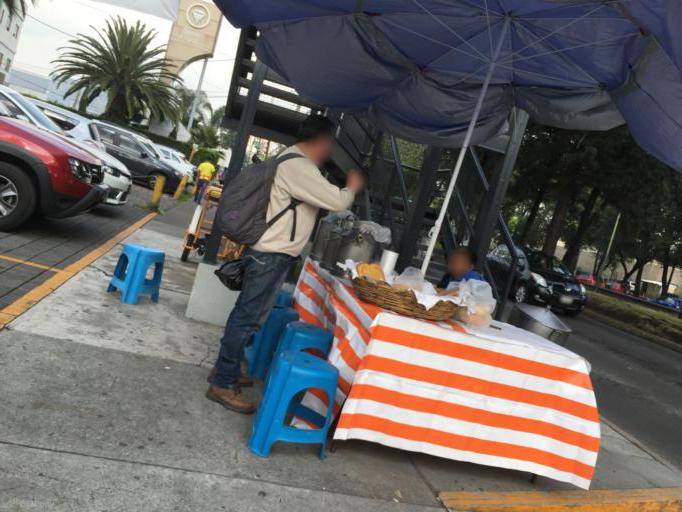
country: MX
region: Mexico City
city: Tlalpan
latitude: 19.2831
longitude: -99.1441
